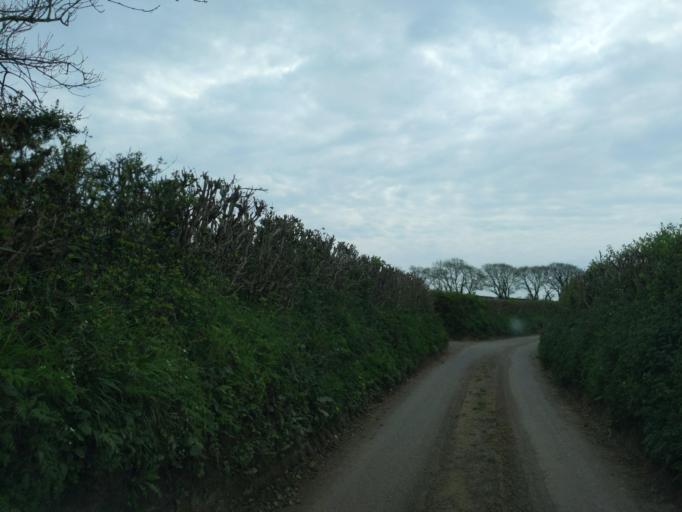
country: GB
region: England
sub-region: Devon
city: Yealmpton
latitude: 50.3553
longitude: -4.0364
